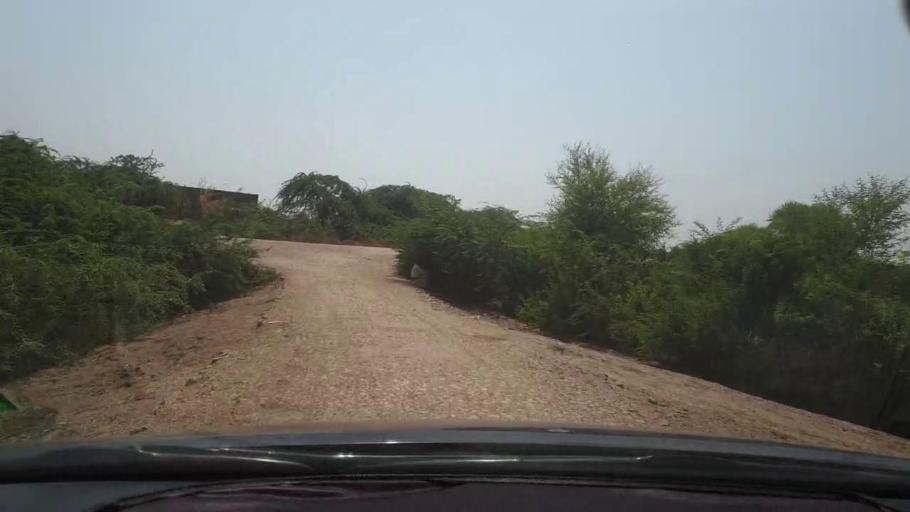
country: PK
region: Sindh
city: Tando Bago
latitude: 24.8014
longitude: 69.1839
